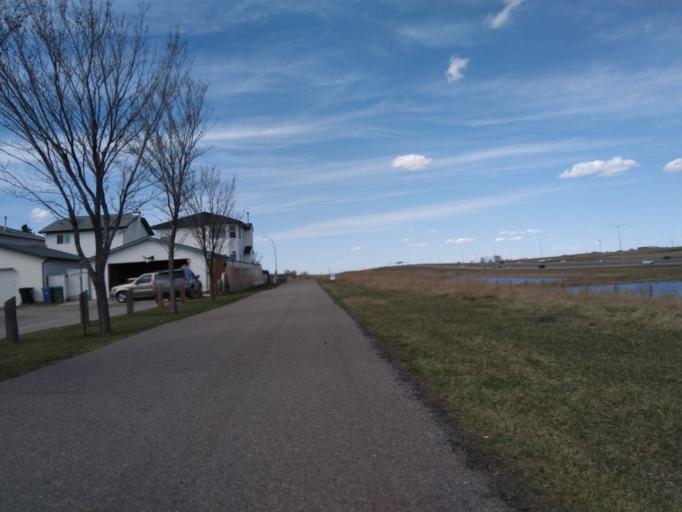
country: CA
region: Alberta
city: Chestermere
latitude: 51.0480
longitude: -113.9229
